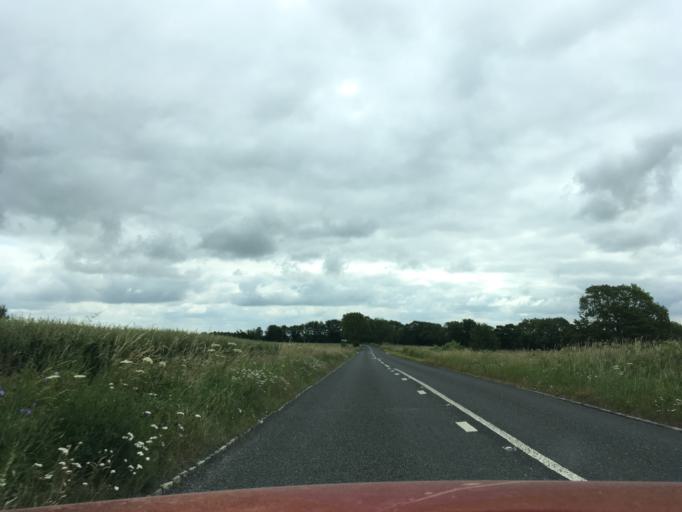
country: GB
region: England
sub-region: Gloucestershire
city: Westfield
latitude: 51.8957
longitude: -1.8870
